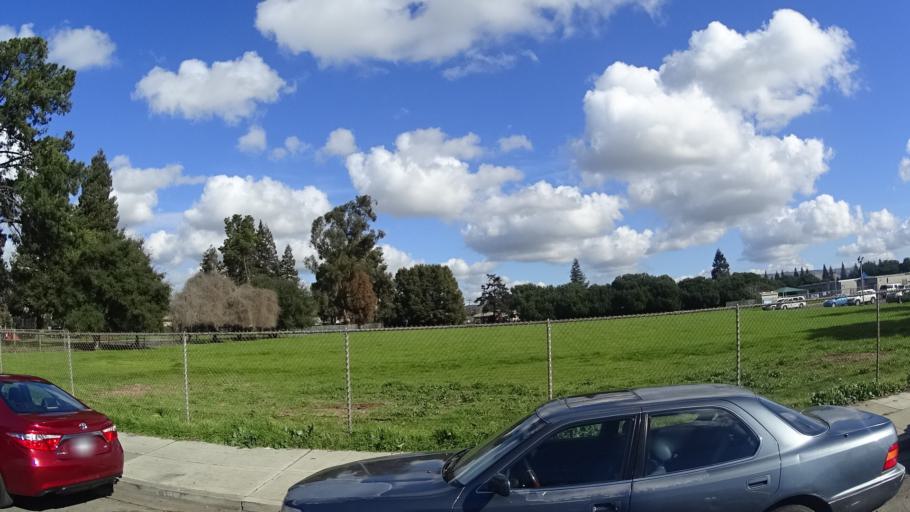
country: US
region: California
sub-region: Alameda County
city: Cherryland
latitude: 37.6571
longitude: -122.1082
